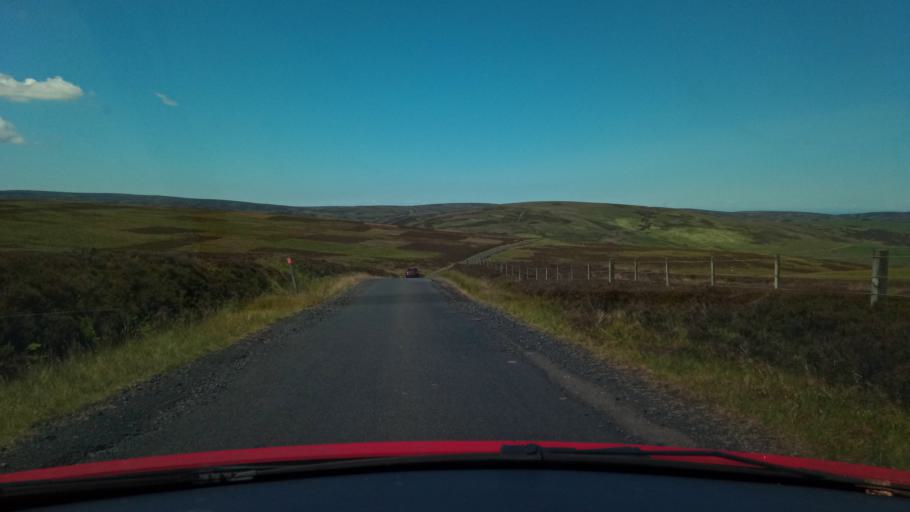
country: GB
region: Scotland
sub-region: East Lothian
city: Dunbar
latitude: 55.8412
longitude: -2.5613
